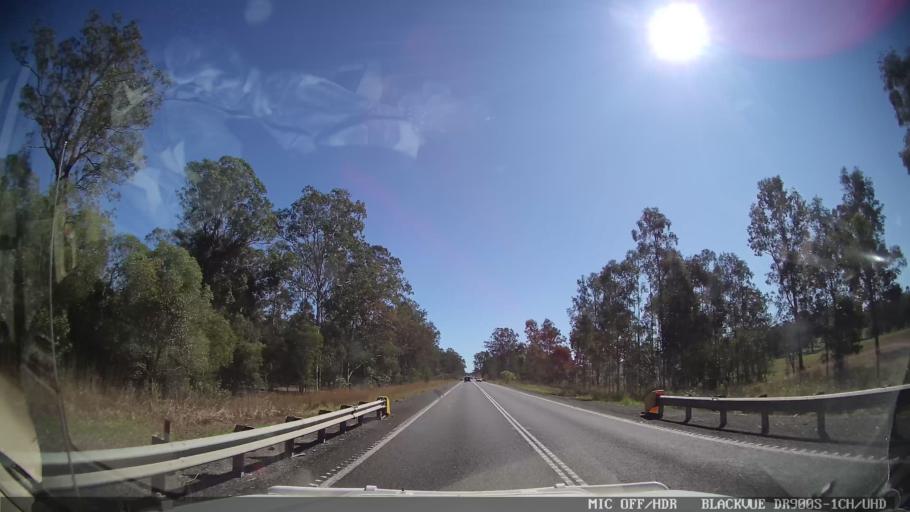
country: AU
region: Queensland
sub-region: Gympie Regional Council
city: Gympie
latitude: -26.0421
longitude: 152.5714
